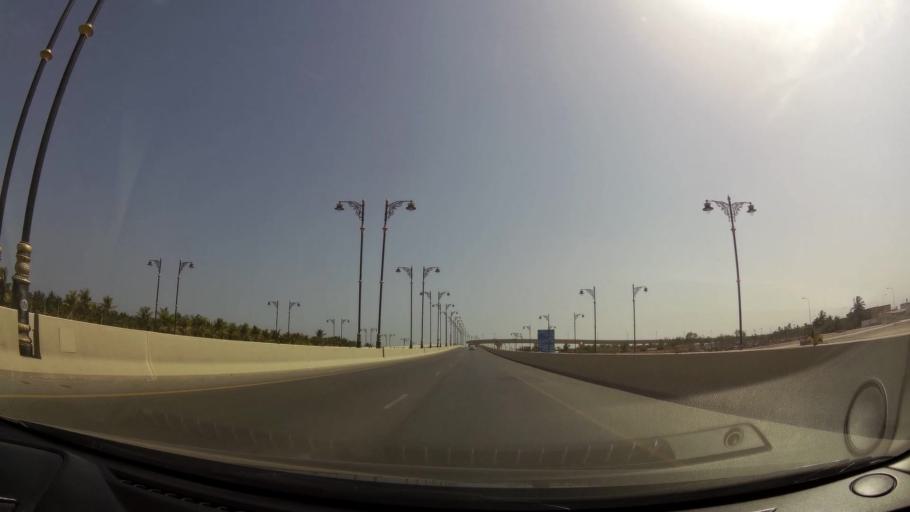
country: OM
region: Zufar
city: Salalah
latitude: 17.0345
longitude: 54.1455
